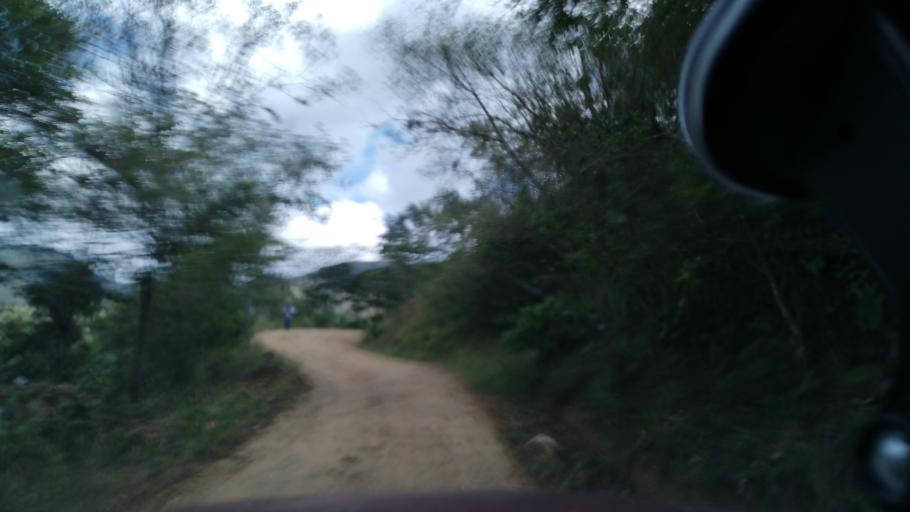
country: CO
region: Cundinamarca
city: Quipile
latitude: 4.8089
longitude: -74.6192
